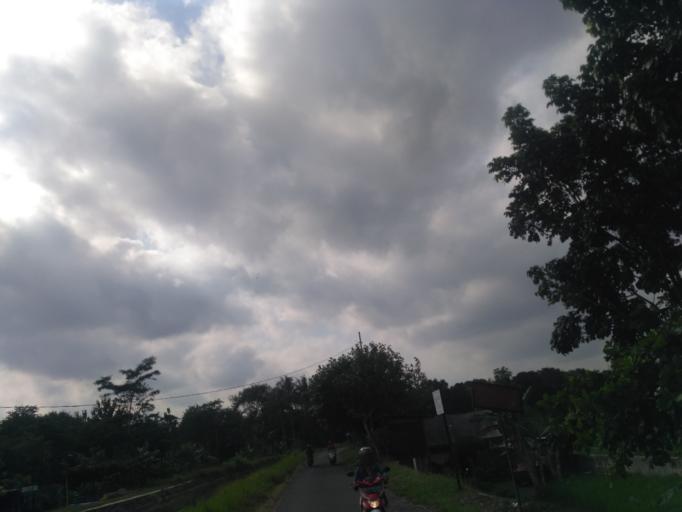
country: ID
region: Daerah Istimewa Yogyakarta
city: Melati
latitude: -7.7524
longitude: 110.3531
